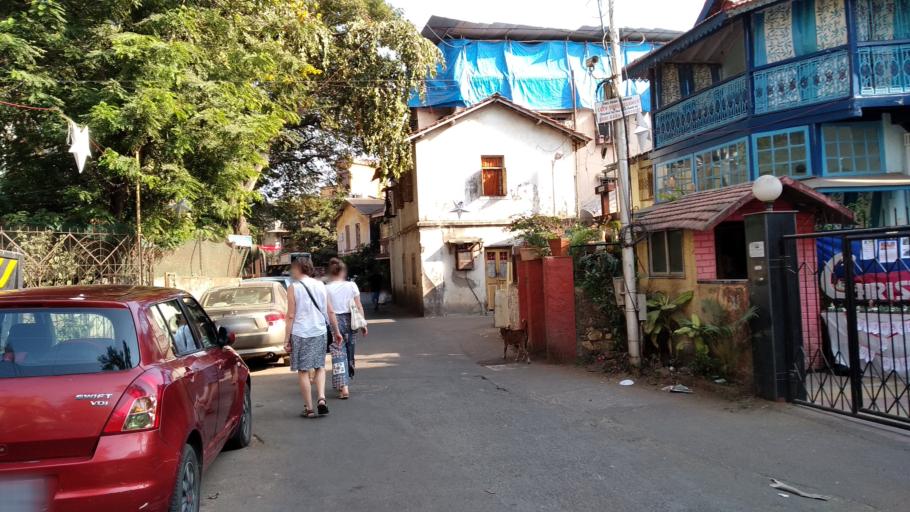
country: IN
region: Maharashtra
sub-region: Mumbai Suburban
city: Mumbai
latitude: 19.0539
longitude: 72.8292
